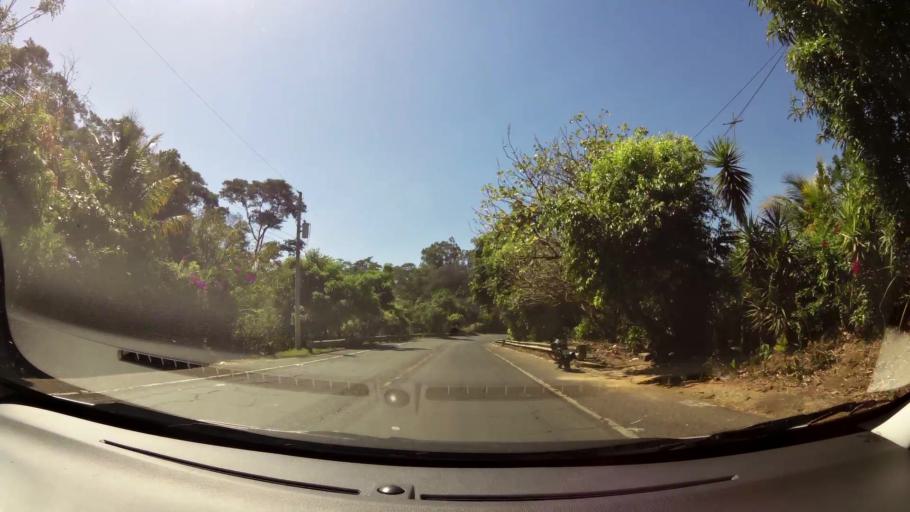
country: SV
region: Ahuachapan
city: Ahuachapan
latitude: 13.9499
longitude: -89.8233
